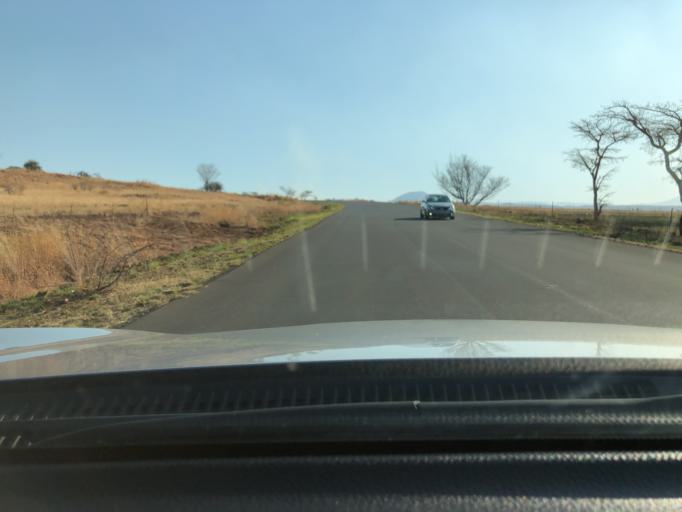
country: ZA
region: KwaZulu-Natal
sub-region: uThukela District Municipality
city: Ekuvukeni
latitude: -28.3628
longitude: 30.0045
